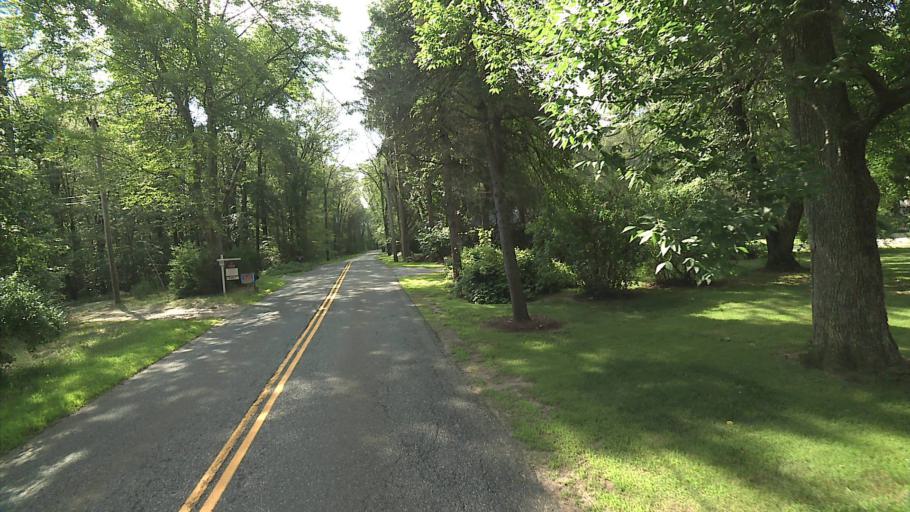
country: US
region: Connecticut
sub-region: Middlesex County
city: Chester Center
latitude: 41.3694
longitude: -72.4976
